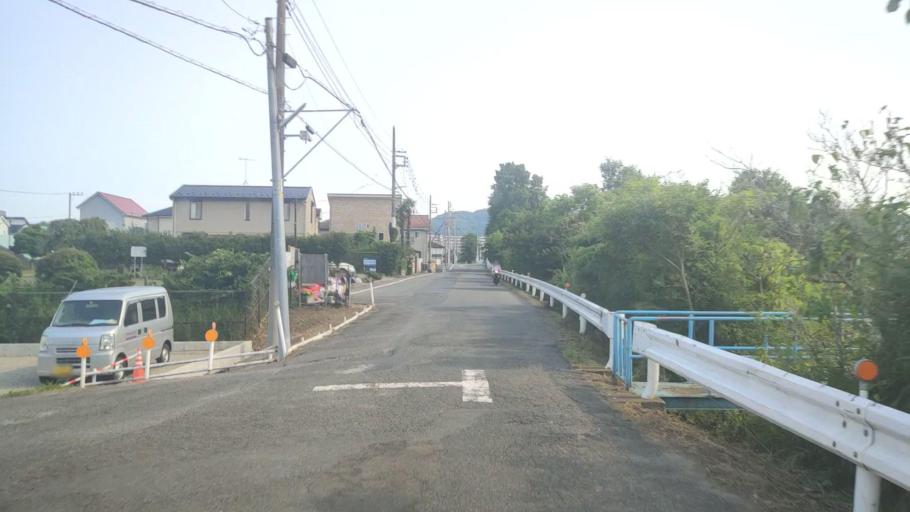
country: JP
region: Kanagawa
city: Hiratsuka
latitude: 35.3415
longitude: 139.3233
